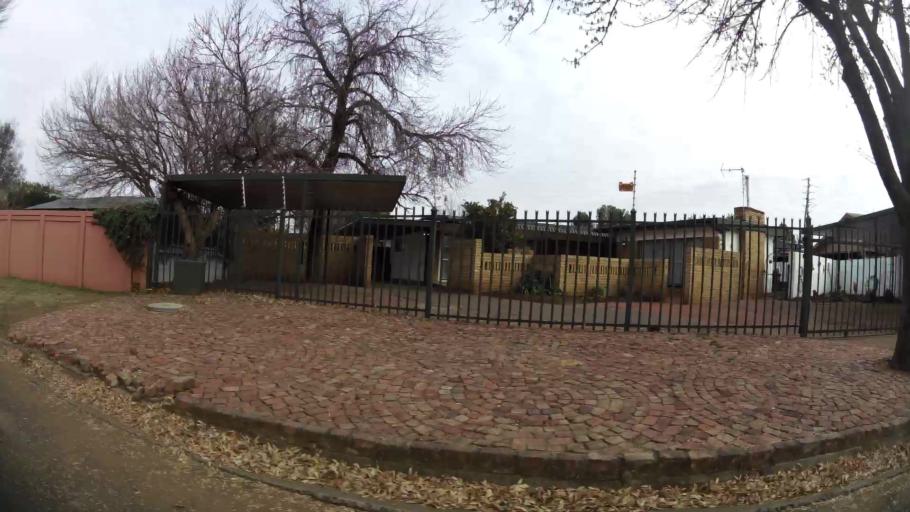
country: ZA
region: Orange Free State
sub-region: Mangaung Metropolitan Municipality
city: Bloemfontein
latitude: -29.1209
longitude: 26.1924
